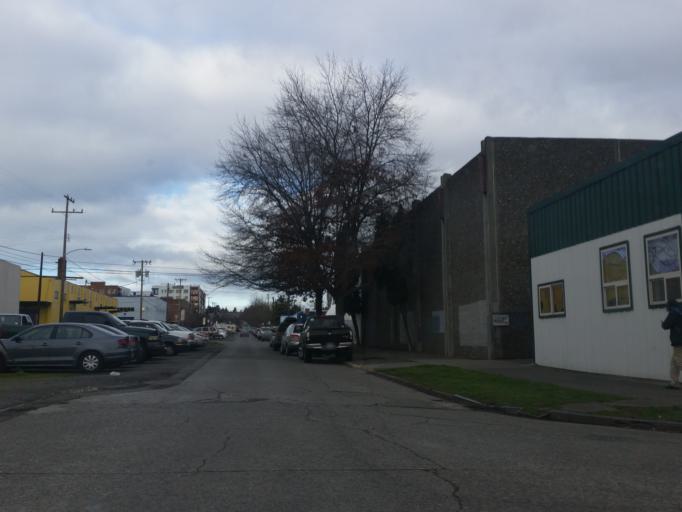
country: US
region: Washington
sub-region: King County
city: Seattle
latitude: 47.6657
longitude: -122.3735
